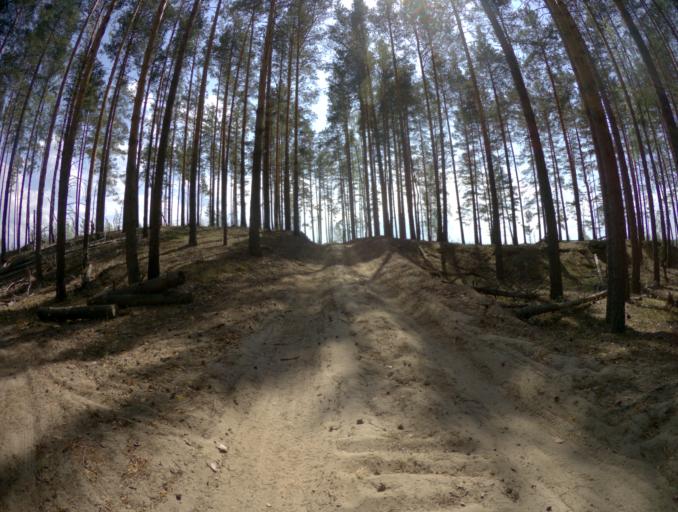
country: RU
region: Ivanovo
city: Talitsy
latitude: 56.4685
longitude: 42.1816
